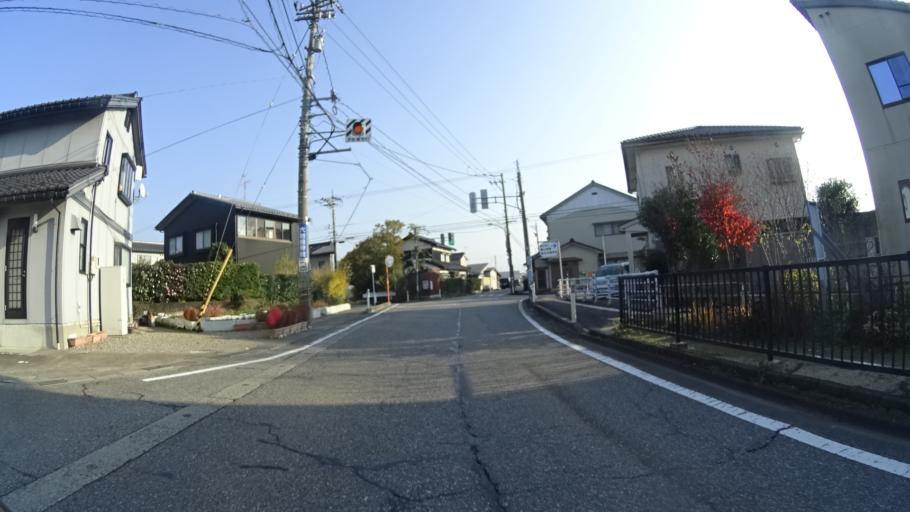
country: JP
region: Toyama
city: Toyama-shi
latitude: 36.6946
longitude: 137.2684
